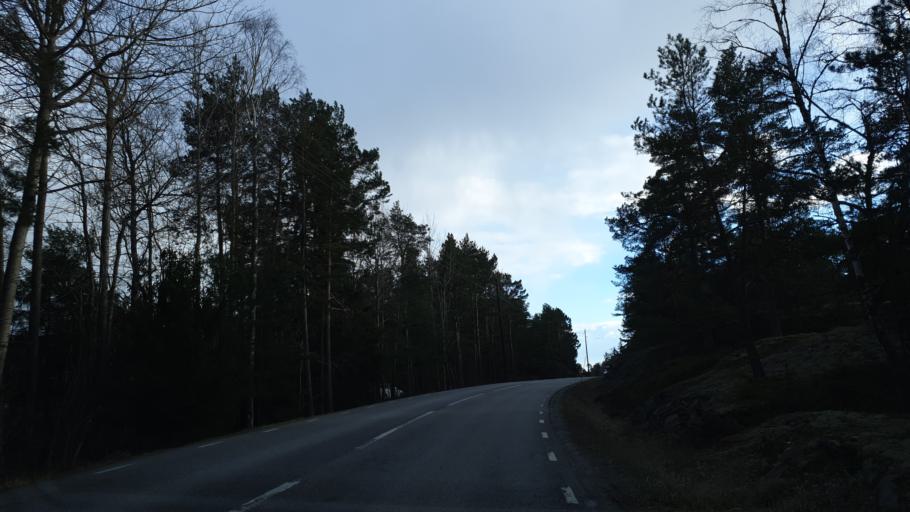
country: SE
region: Stockholm
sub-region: Varmdo Kommun
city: Holo
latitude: 59.3416
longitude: 18.7184
